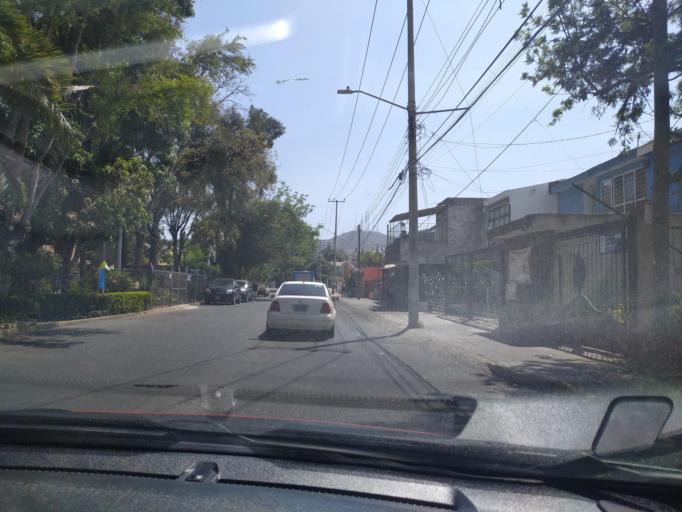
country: MX
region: Jalisco
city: Las Pintas de Arriba
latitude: 20.6208
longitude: -103.3474
